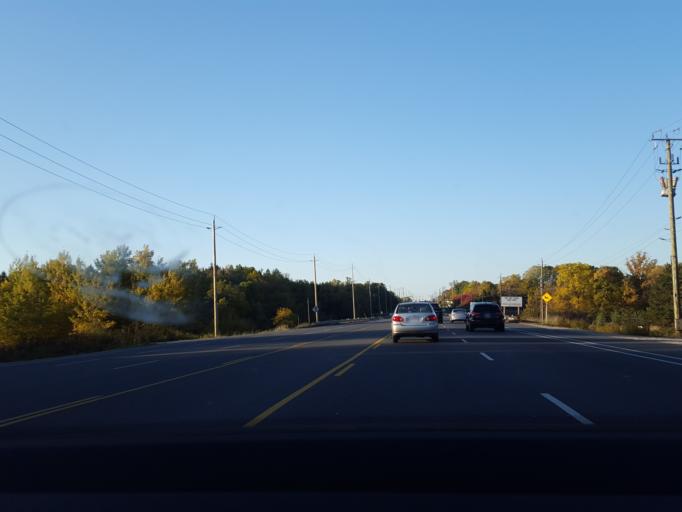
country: CA
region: Ontario
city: Newmarket
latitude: 44.0200
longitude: -79.4723
